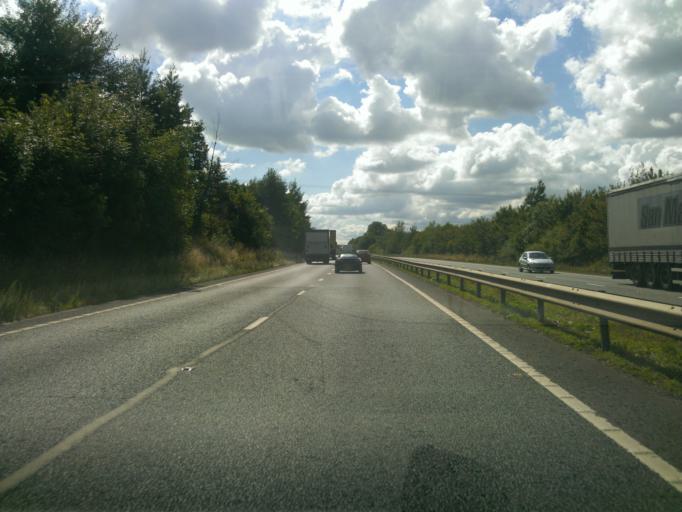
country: GB
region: England
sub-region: Leicestershire
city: Market Harborough
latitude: 52.4064
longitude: -0.9641
